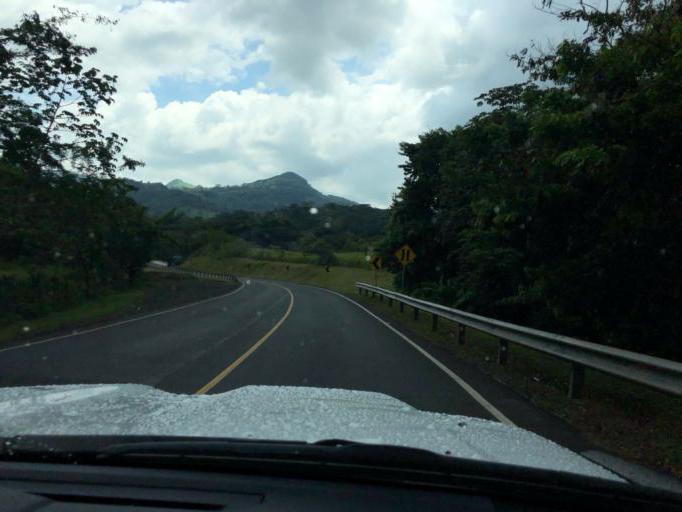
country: NI
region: Chontales
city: Villa Sandino
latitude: 12.0024
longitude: -84.9374
